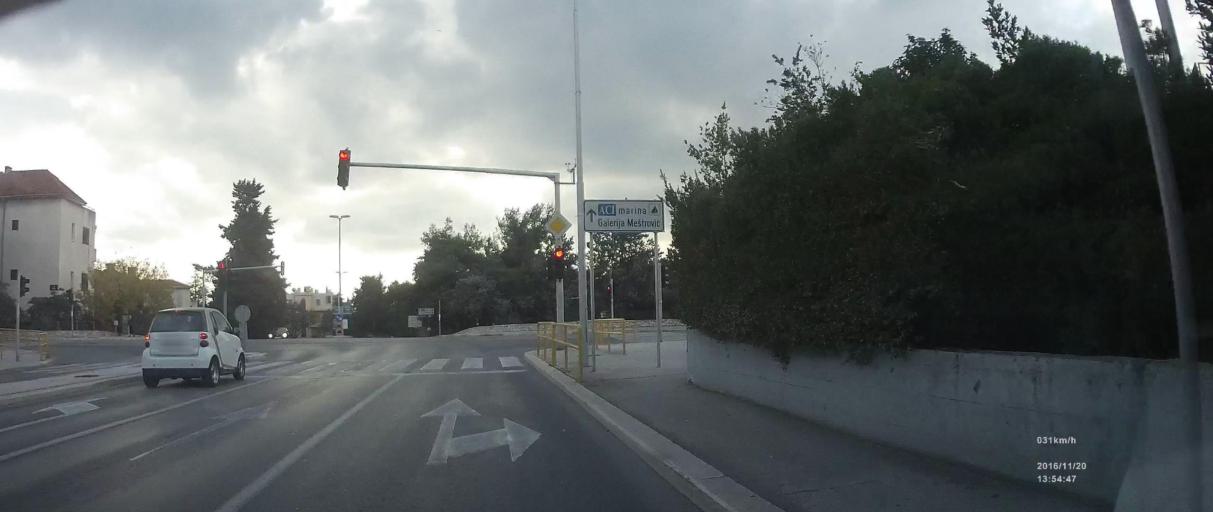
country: HR
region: Splitsko-Dalmatinska
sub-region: Grad Split
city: Split
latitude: 43.5052
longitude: 16.4235
